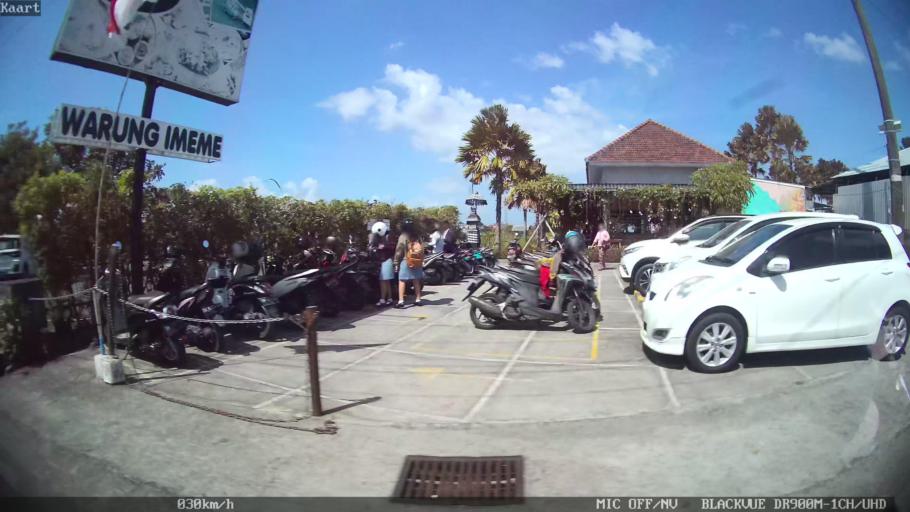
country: ID
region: Bali
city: Banjar Kertasari
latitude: -8.6318
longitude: 115.1782
